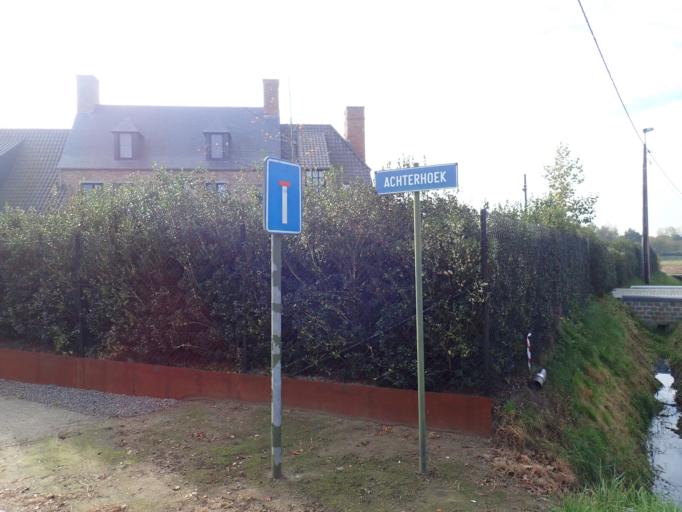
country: BE
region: Flanders
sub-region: Provincie Antwerpen
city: Berlaar
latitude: 51.1264
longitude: 4.6641
